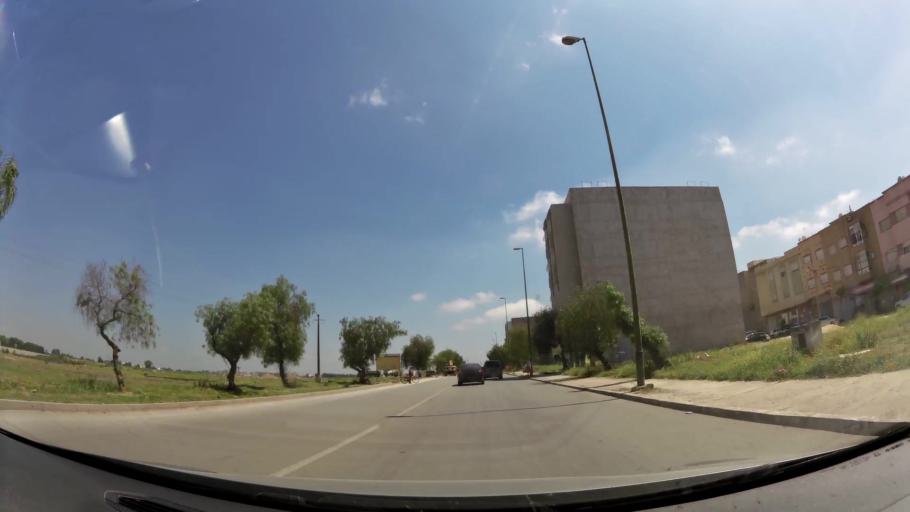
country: MA
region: Fes-Boulemane
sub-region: Fes
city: Fes
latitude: 34.0038
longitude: -5.0443
